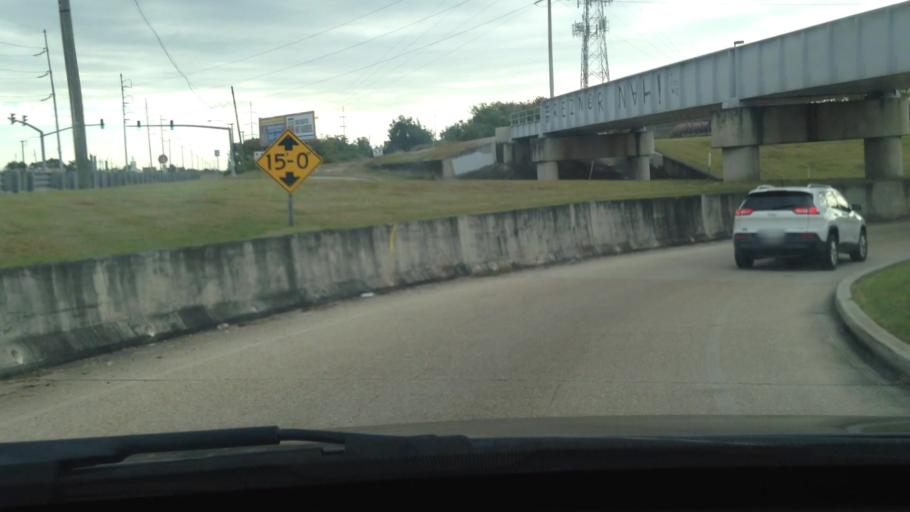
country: US
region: Louisiana
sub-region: Jefferson Parish
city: Jefferson
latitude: 29.9722
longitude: -90.1279
